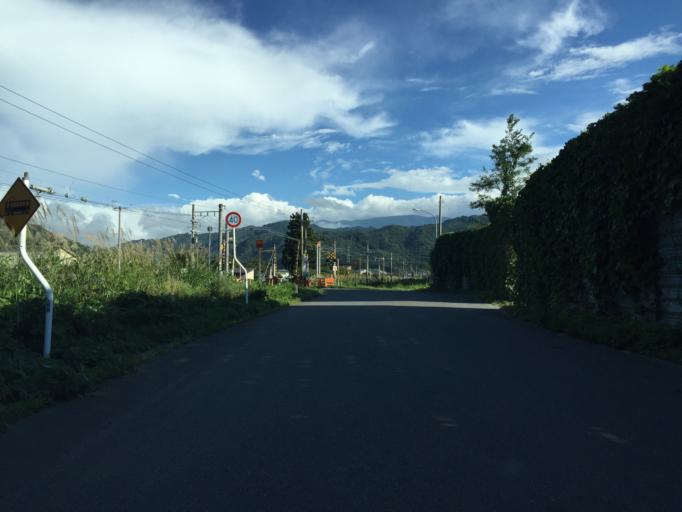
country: JP
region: Yamagata
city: Yonezawa
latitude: 37.8747
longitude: 140.1396
